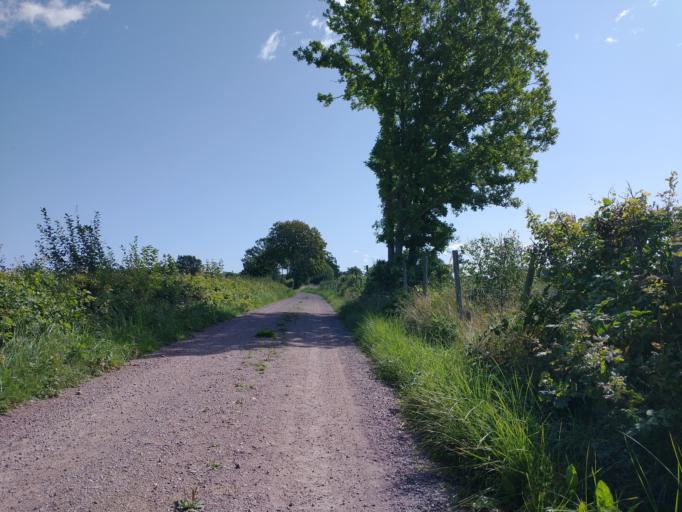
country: SE
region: Kalmar
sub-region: Kalmar Kommun
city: Lindsdal
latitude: 56.7920
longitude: 16.2933
